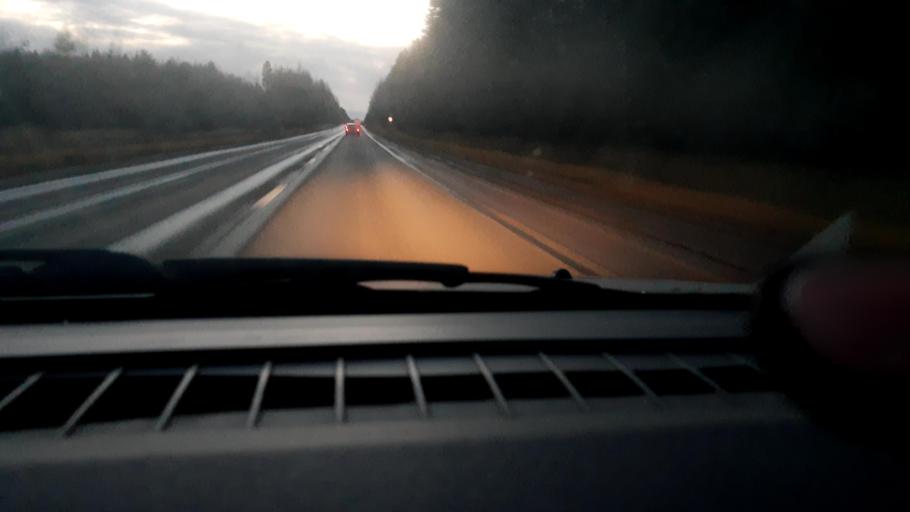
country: RU
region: Nizjnij Novgorod
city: Vladimirskoye
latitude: 56.8806
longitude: 44.9705
